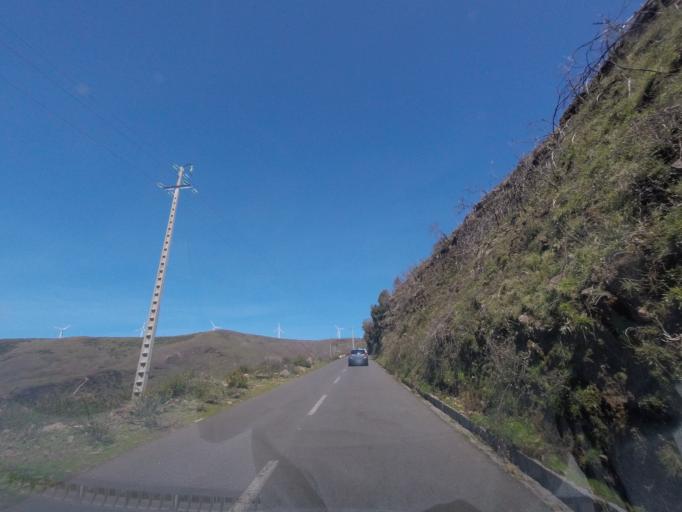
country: PT
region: Madeira
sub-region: Calheta
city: Arco da Calheta
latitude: 32.7353
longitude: -17.1045
